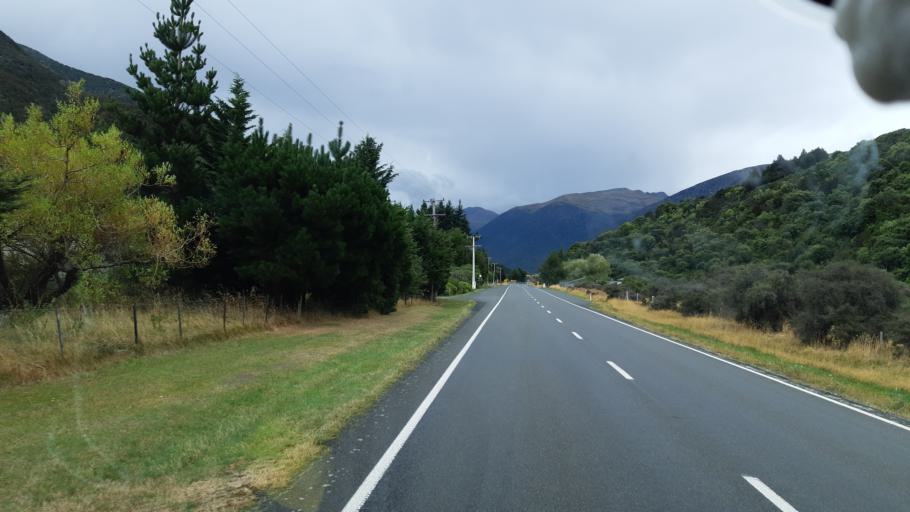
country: NZ
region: Canterbury
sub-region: Hurunui District
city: Amberley
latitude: -42.5667
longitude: 172.3581
